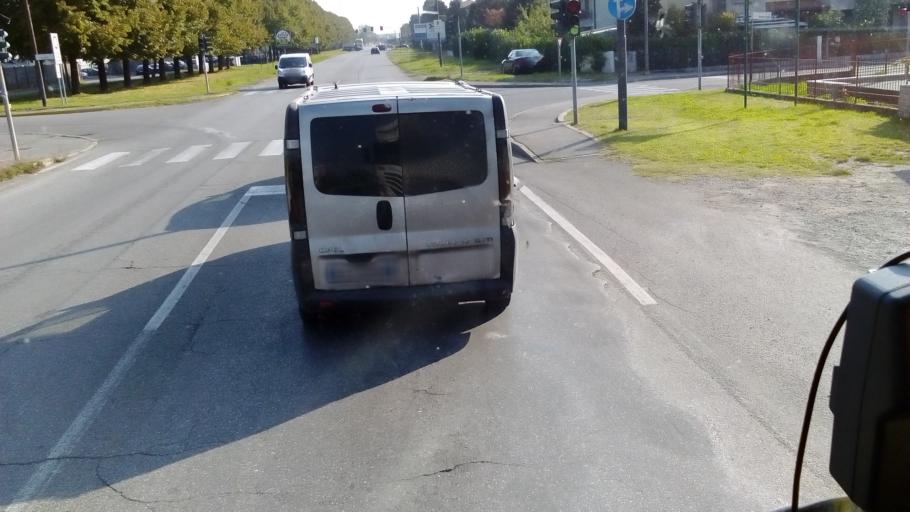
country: IT
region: Lombardy
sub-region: Provincia di Bergamo
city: Ciserano
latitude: 45.5888
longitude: 9.5987
